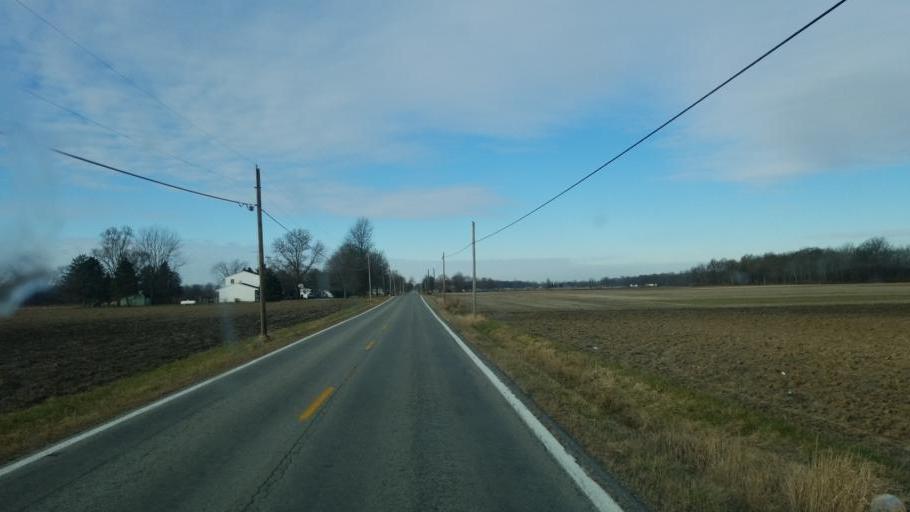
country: US
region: Ohio
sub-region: Marion County
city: Marion
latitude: 40.5494
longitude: -83.0524
